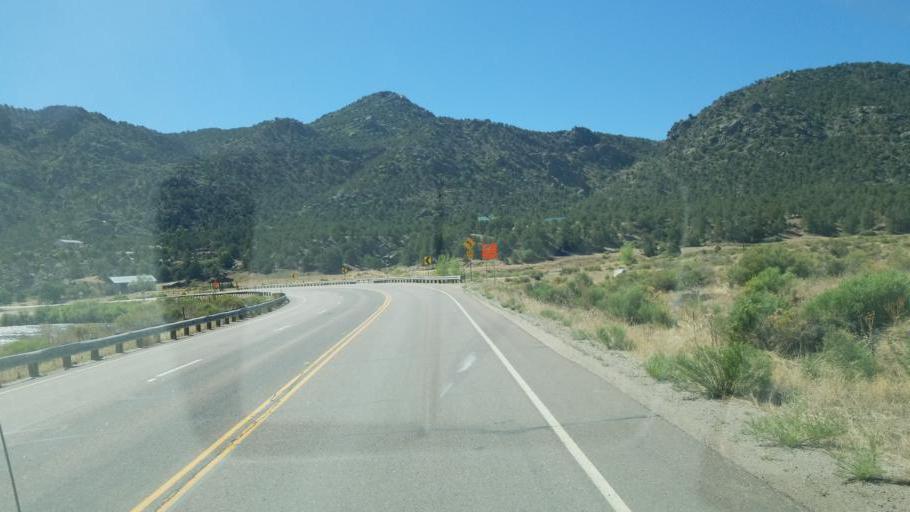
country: US
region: Colorado
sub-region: Custer County
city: Westcliffe
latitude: 38.3939
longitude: -105.6277
